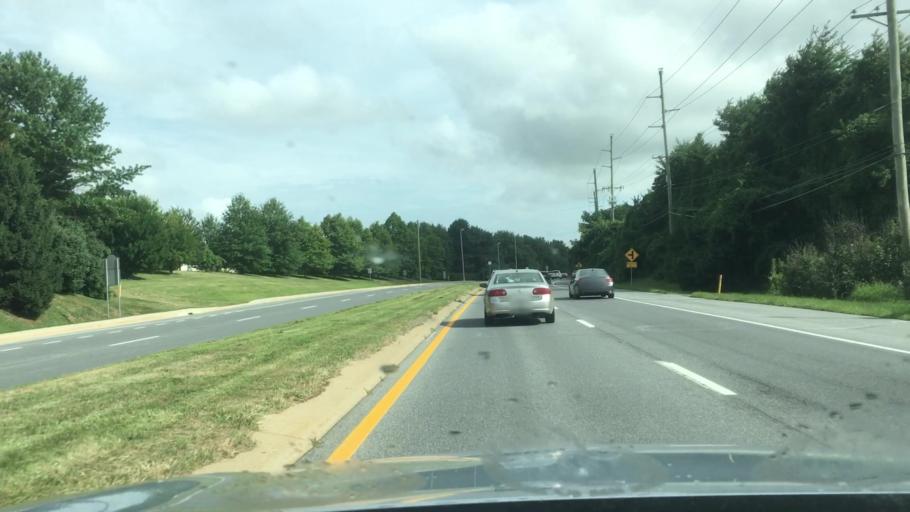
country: US
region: Delaware
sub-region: New Castle County
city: North Star
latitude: 39.7635
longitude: -75.7049
